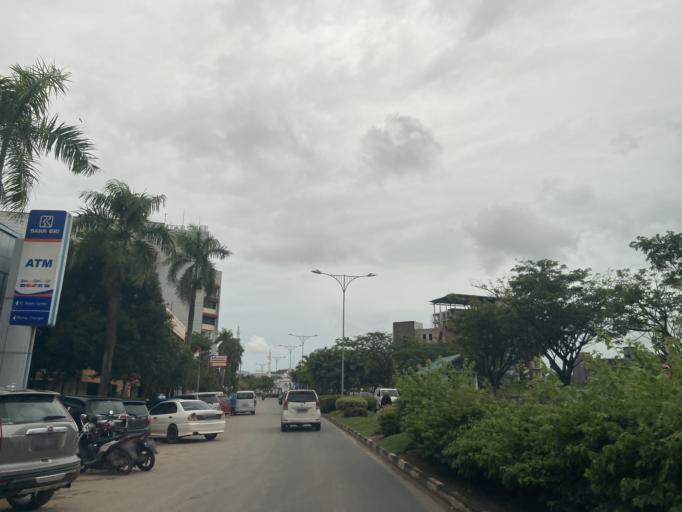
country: SG
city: Singapore
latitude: 1.1308
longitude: 104.0509
